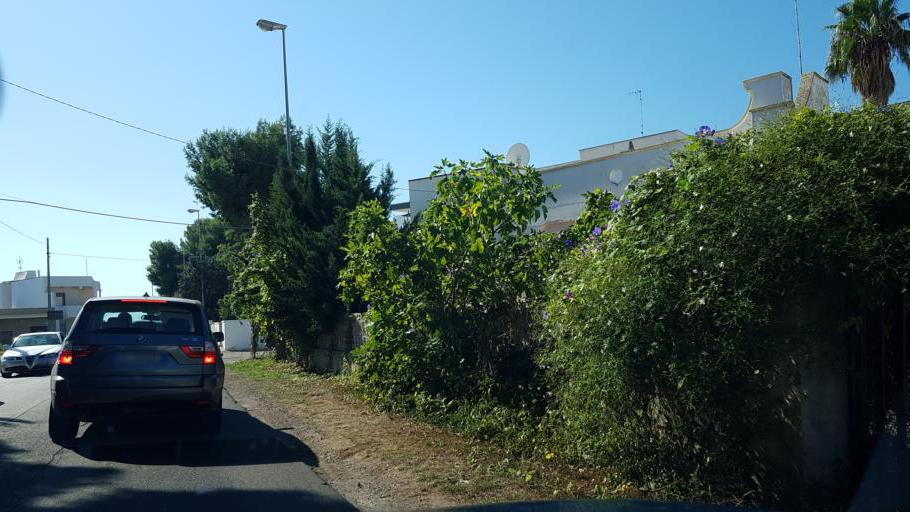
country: IT
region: Apulia
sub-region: Provincia di Lecce
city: Porto Cesareo
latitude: 40.2579
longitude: 17.9046
